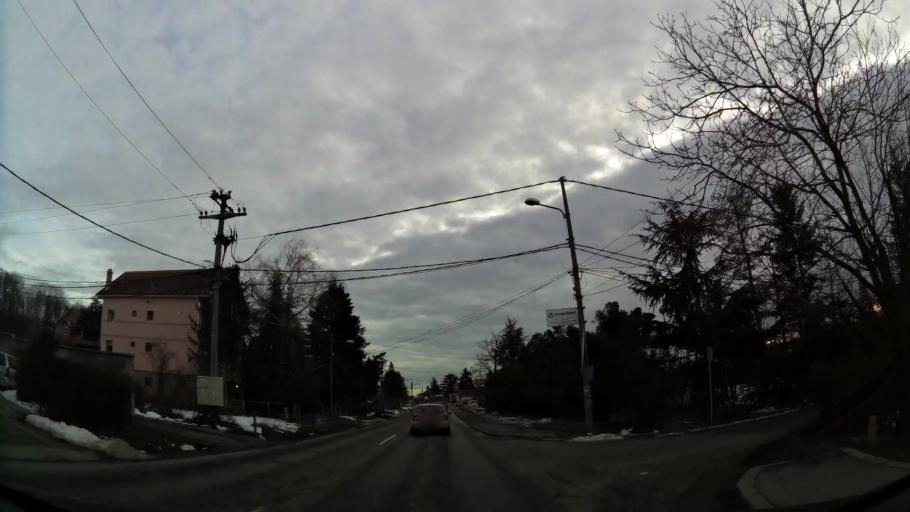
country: RS
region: Central Serbia
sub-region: Belgrade
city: Rakovica
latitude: 44.7335
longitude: 20.4832
